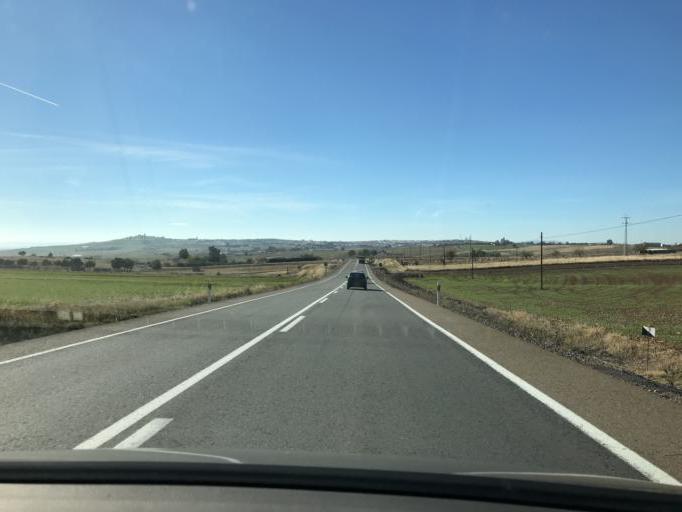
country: ES
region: Extremadura
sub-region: Provincia de Badajoz
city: Azuaga
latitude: 38.2880
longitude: -5.6570
